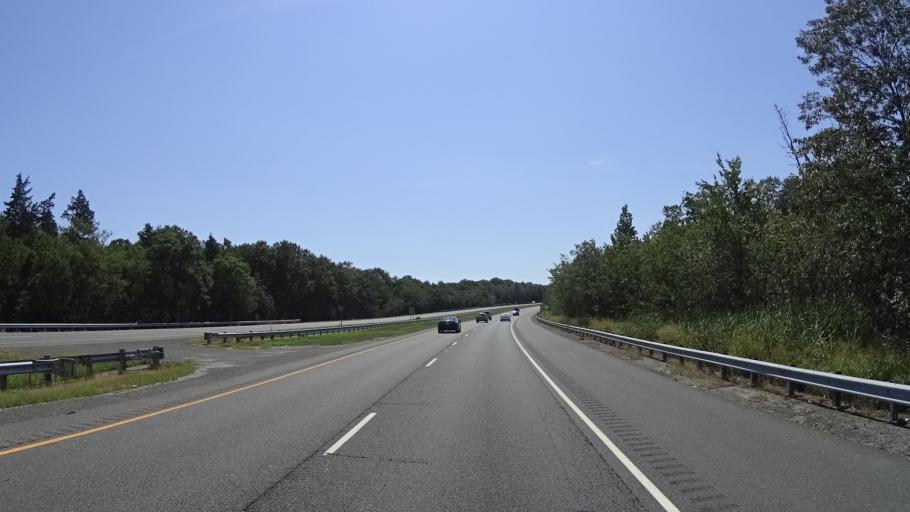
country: US
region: New Jersey
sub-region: Monmouth County
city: Eatontown
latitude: 40.2718
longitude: -74.0644
